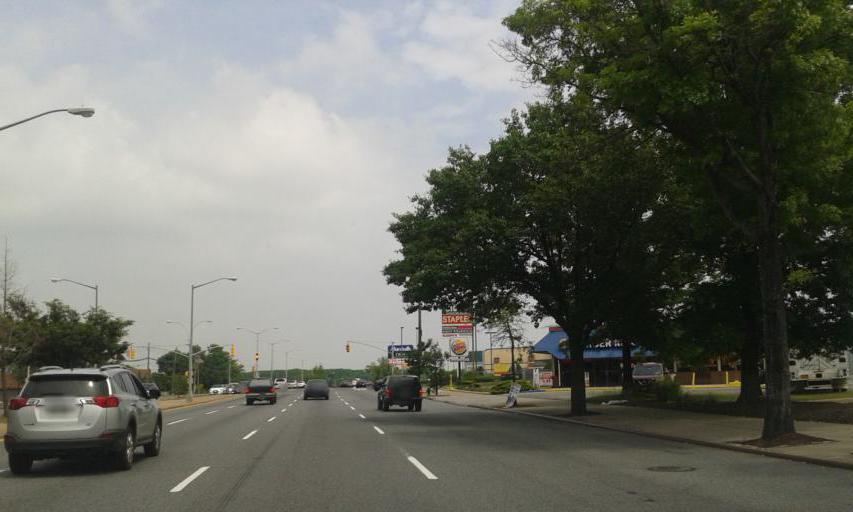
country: US
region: New York
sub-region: Richmond County
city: Bloomfield
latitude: 40.5847
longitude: -74.1686
